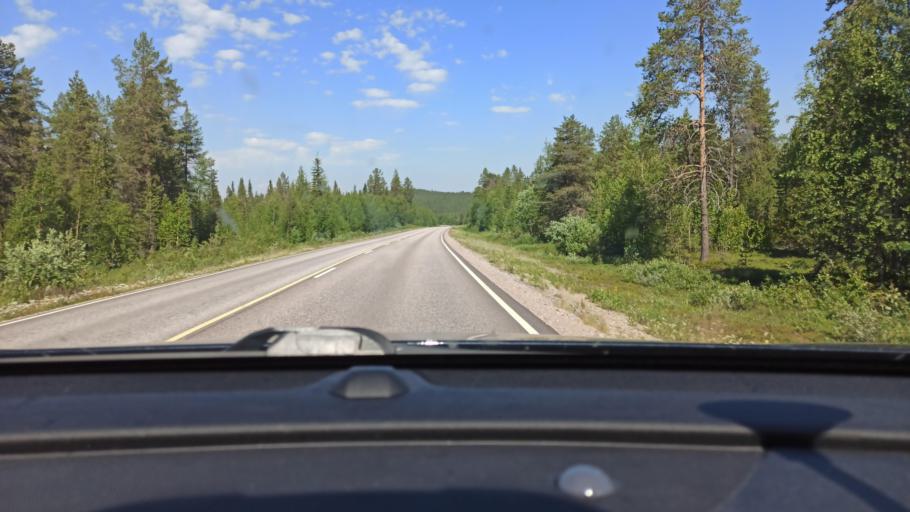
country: FI
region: Lapland
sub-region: Tunturi-Lappi
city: Muonio
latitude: 67.9989
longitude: 23.6137
